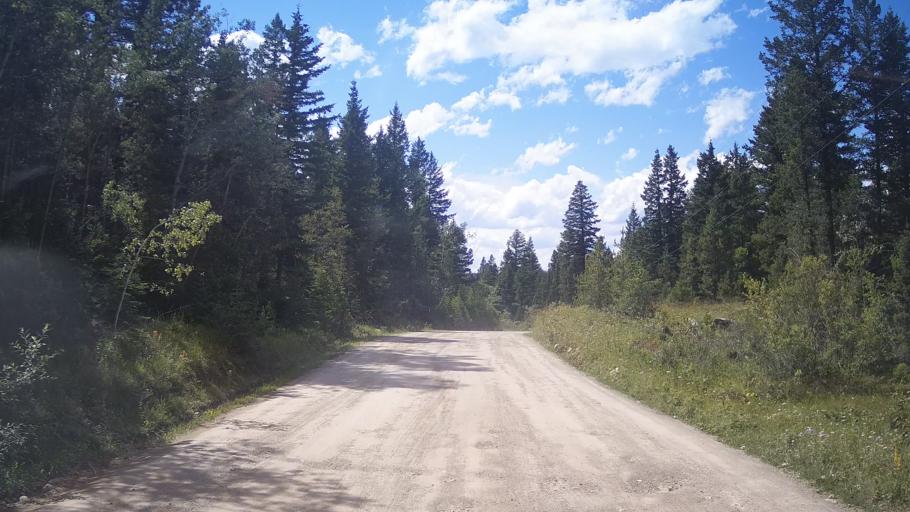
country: CA
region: British Columbia
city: Lillooet
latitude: 51.2657
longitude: -121.9686
